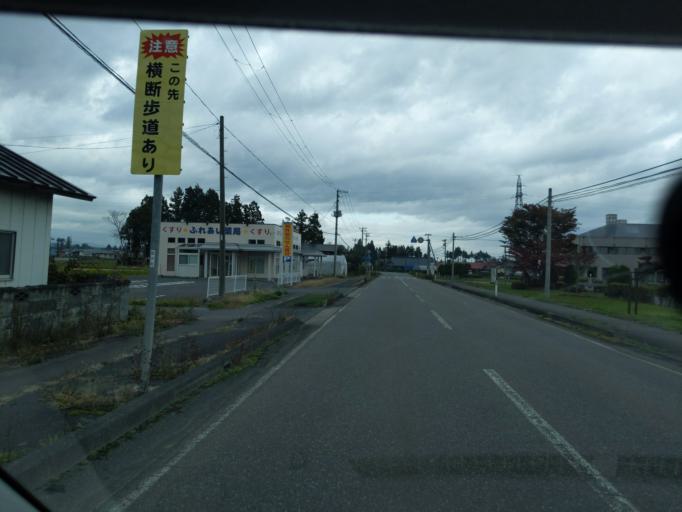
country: JP
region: Iwate
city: Mizusawa
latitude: 39.1278
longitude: 141.0672
